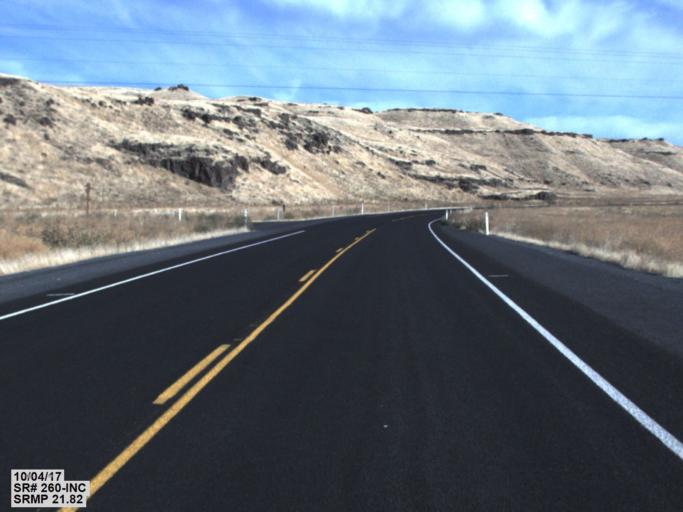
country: US
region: Washington
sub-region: Franklin County
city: Connell
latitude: 46.6459
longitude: -118.6142
